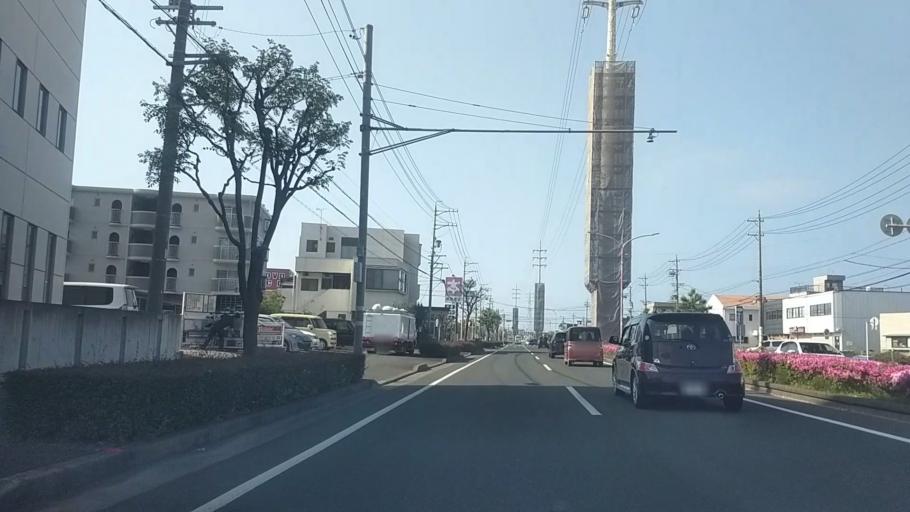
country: JP
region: Shizuoka
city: Hamamatsu
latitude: 34.7070
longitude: 137.7582
